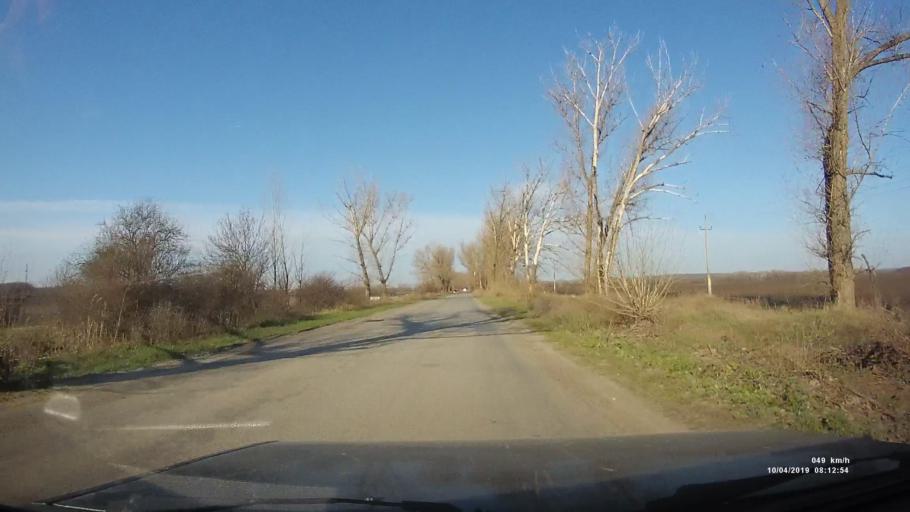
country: RU
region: Rostov
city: Masalovka
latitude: 48.3619
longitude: 40.2524
